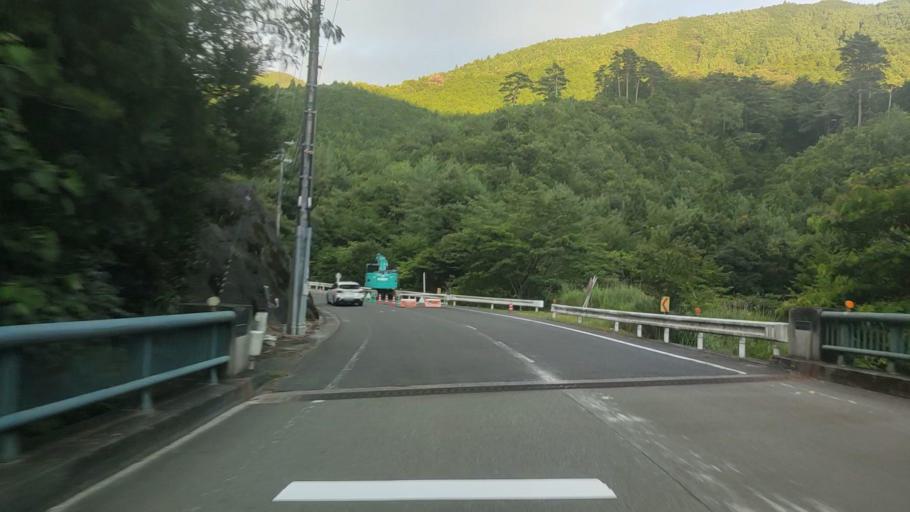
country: JP
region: Wakayama
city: Tanabe
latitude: 33.8299
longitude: 135.6487
